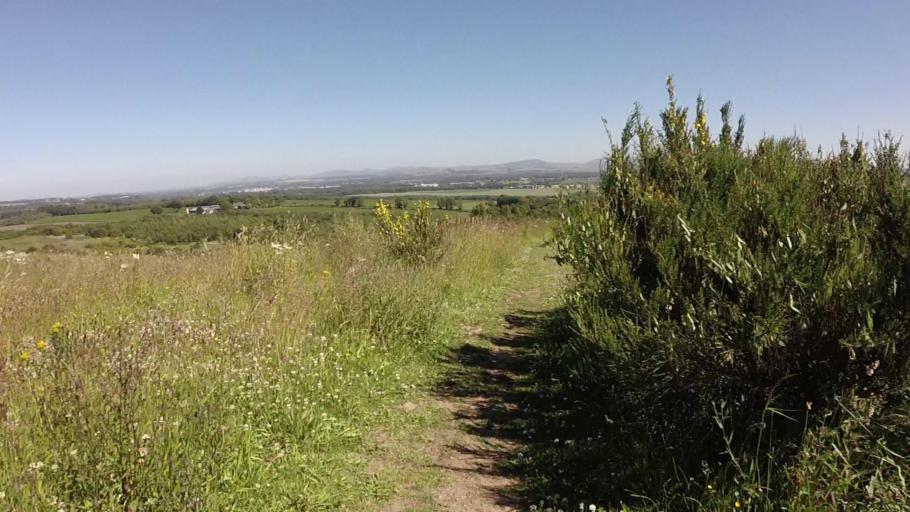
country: GB
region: Scotland
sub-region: West Lothian
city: West Calder
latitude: 55.8831
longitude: -3.5928
